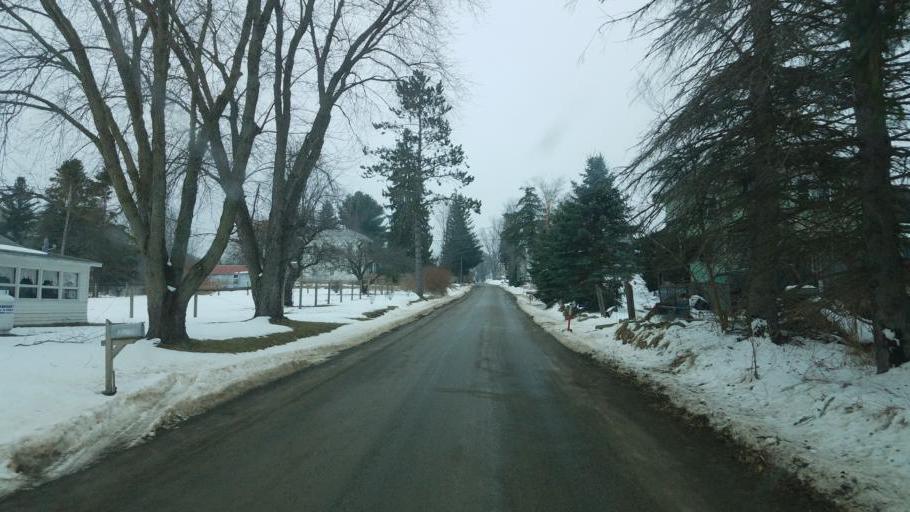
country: US
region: New York
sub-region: Allegany County
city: Andover
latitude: 41.9907
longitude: -77.7623
